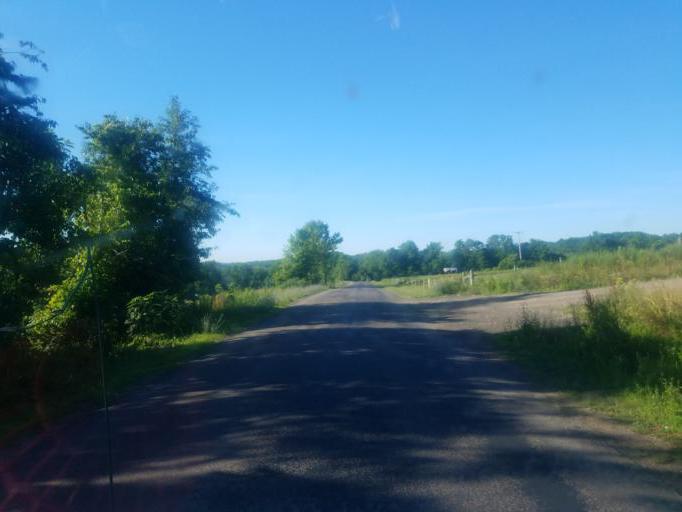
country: US
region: New York
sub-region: Wayne County
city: Lyons
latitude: 43.1213
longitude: -77.0385
